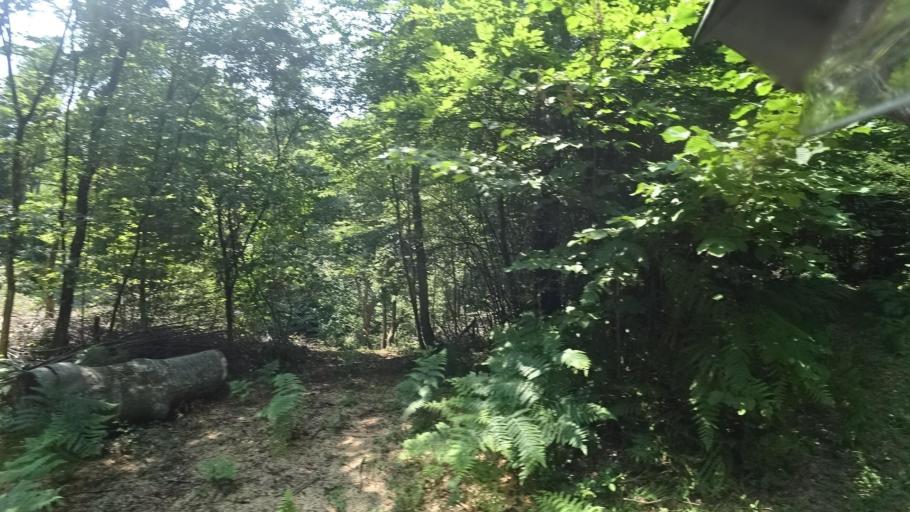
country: HR
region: Karlovacka
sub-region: Grad Ogulin
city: Ogulin
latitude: 45.3114
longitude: 15.1700
